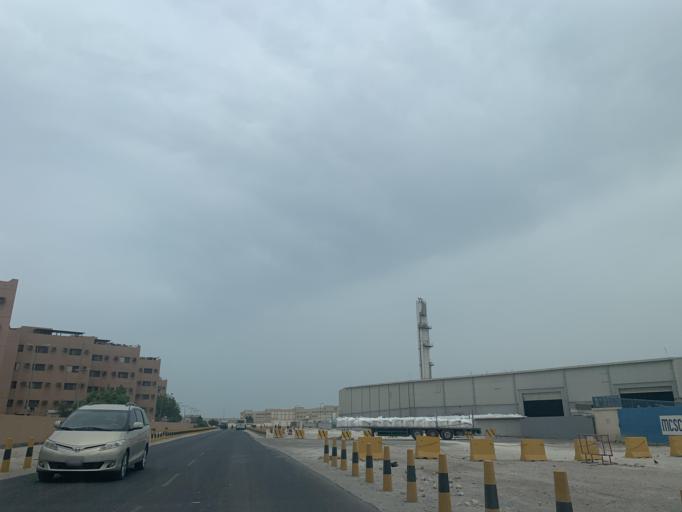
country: BH
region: Muharraq
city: Al Hadd
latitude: 26.2087
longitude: 50.6757
